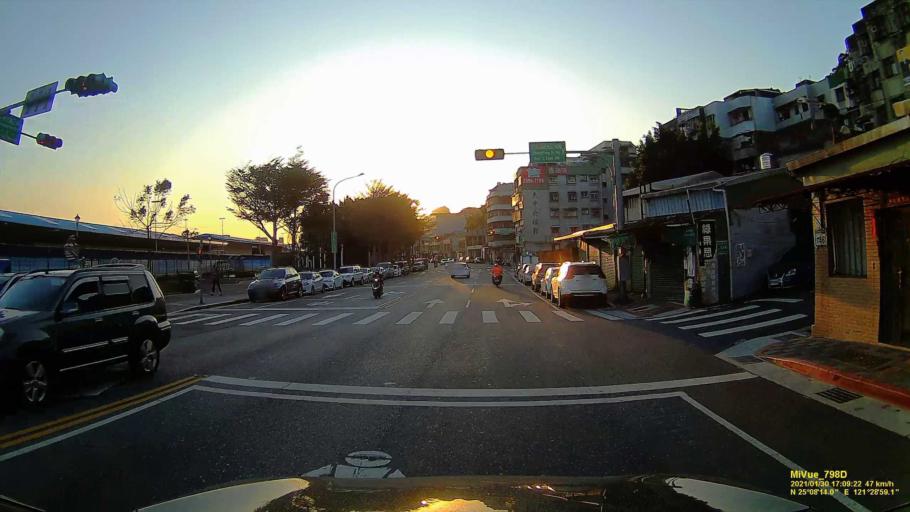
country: TW
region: Taipei
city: Taipei
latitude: 25.1372
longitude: 121.4829
